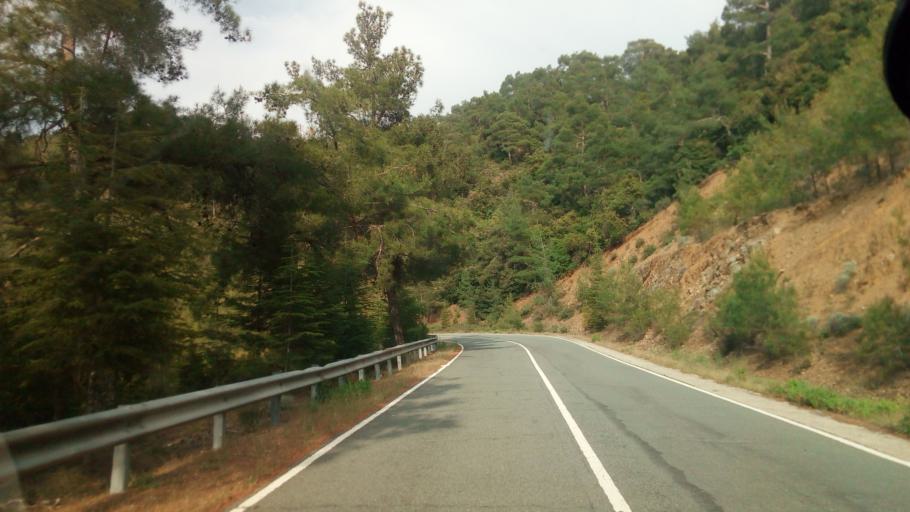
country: CY
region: Lefkosia
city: Kakopetria
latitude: 34.9926
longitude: 32.7911
